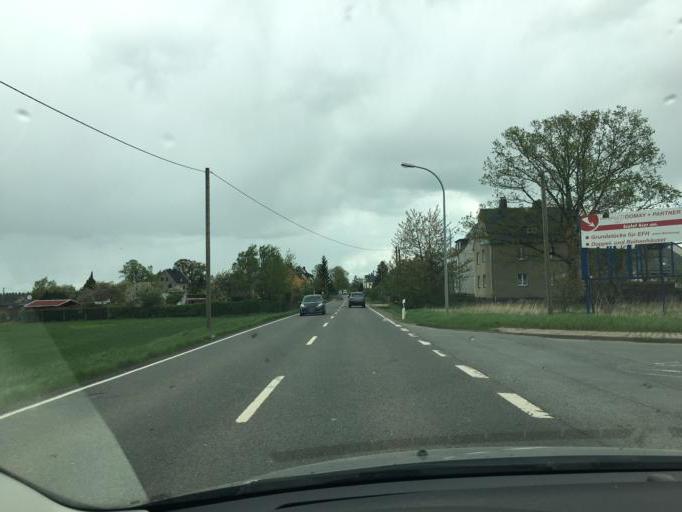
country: DE
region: Saxony
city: Limbach-Oberfrohna
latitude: 50.8425
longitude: 12.7693
